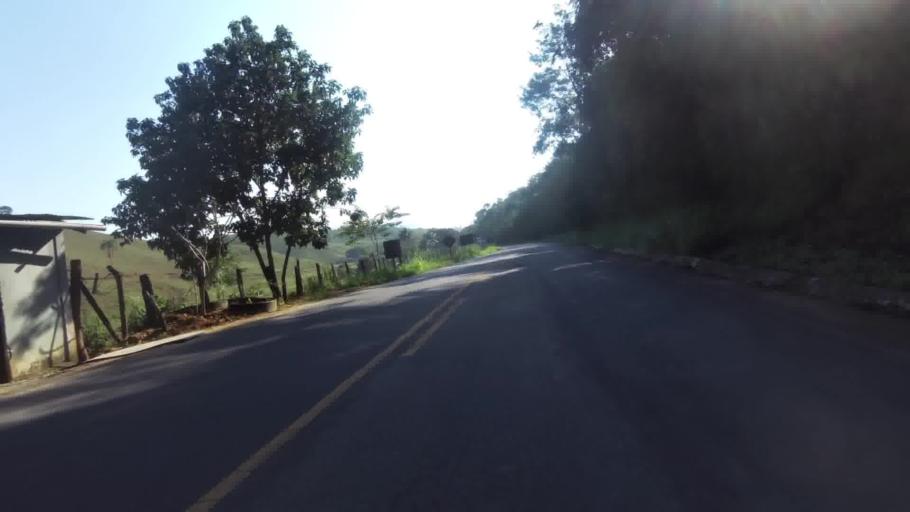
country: BR
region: Espirito Santo
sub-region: Alfredo Chaves
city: Alfredo Chaves
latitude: -20.6864
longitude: -40.7077
